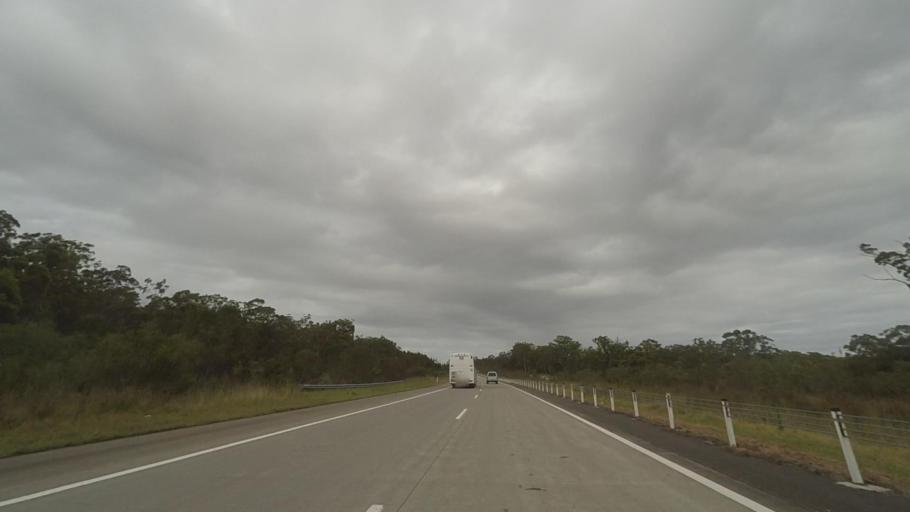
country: AU
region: New South Wales
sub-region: Port Stephens Shire
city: Port Stephens
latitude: -32.6226
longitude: 152.0639
